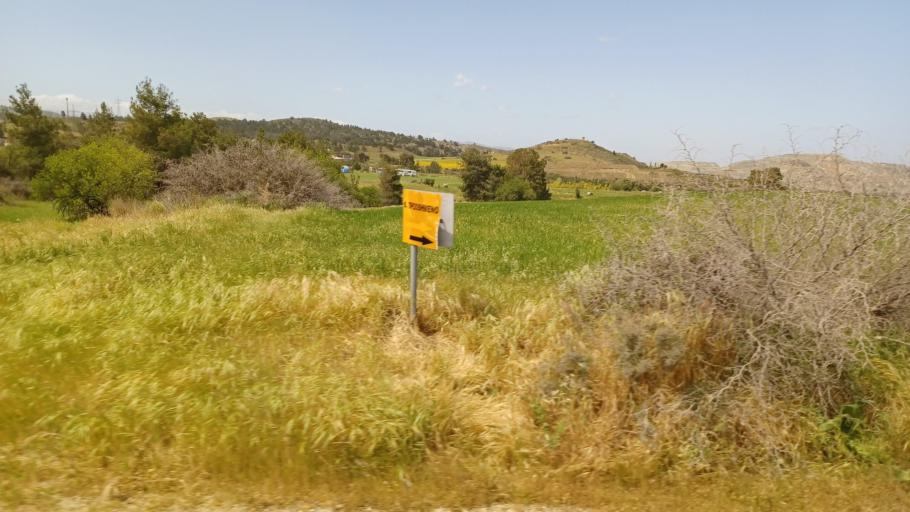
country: CY
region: Lefkosia
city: Lefka
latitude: 35.0736
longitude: 32.9297
